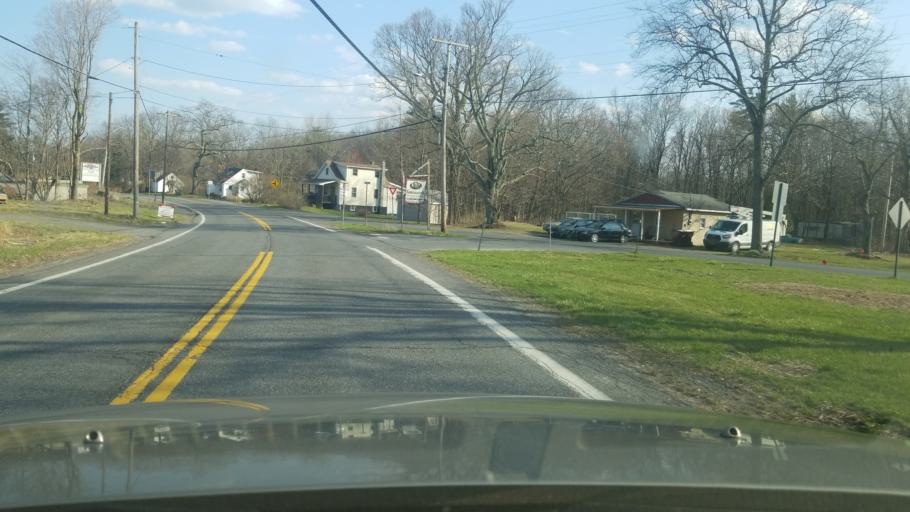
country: US
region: New York
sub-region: Greene County
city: Palenville
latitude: 42.1674
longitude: -74.0165
